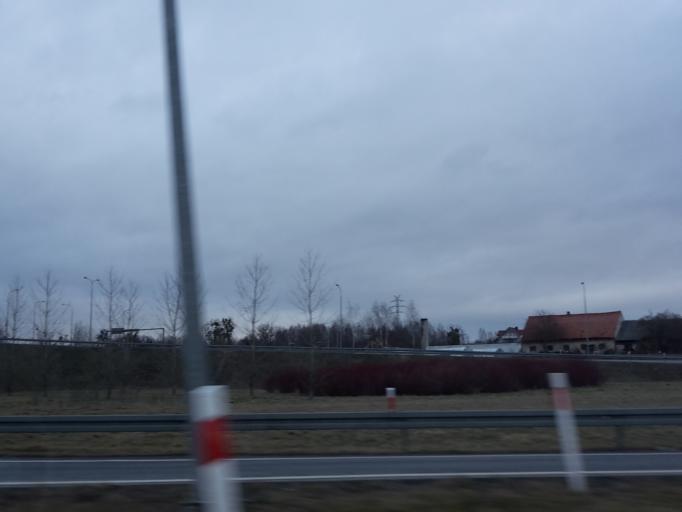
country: PL
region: Warmian-Masurian Voivodeship
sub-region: Powiat elblaski
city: Gronowo Gorne
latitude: 54.1377
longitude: 19.4510
